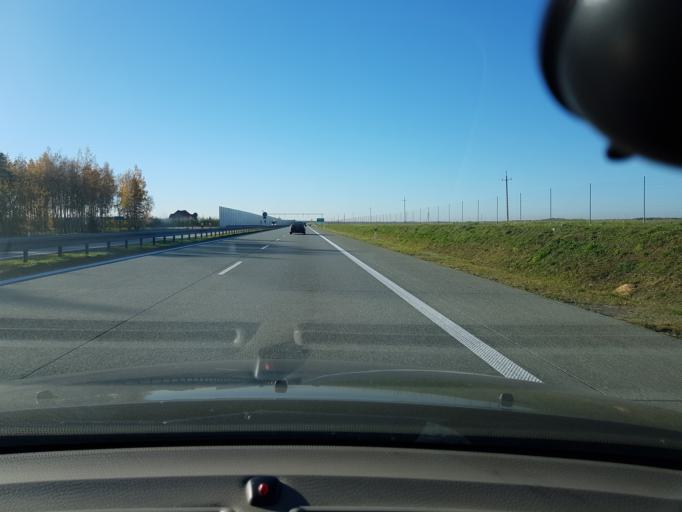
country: PL
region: Lodz Voivodeship
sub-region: Powiat skierniewicki
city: Kowiesy
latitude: 51.8588
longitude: 20.3778
